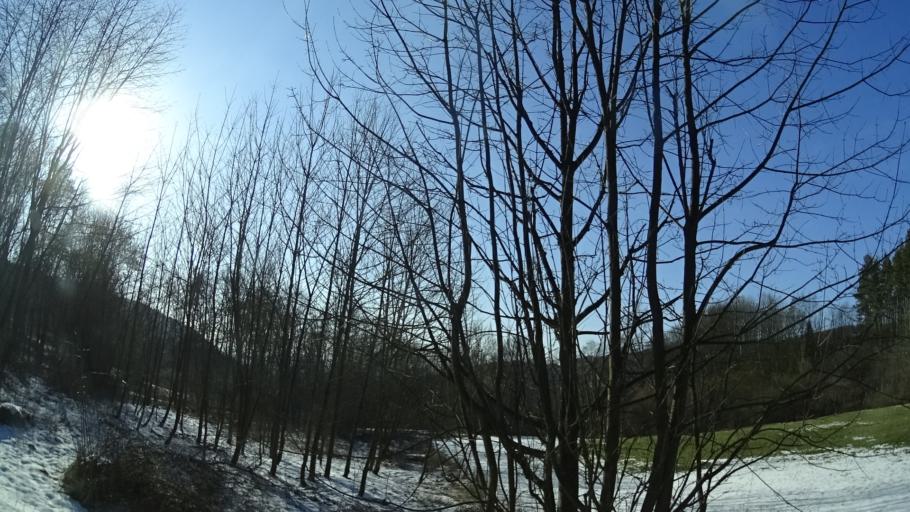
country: DE
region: Hesse
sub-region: Regierungsbezirk Kassel
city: Flieden
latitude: 50.3737
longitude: 9.5922
